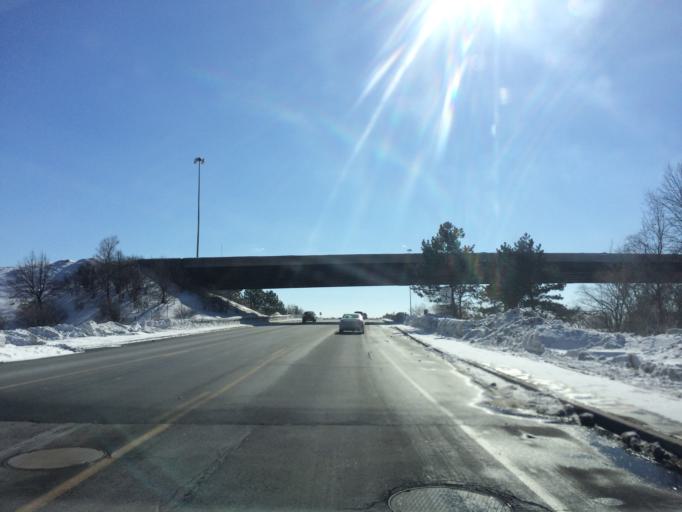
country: US
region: New York
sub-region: Monroe County
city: Rochester
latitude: 43.1114
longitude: -77.5977
